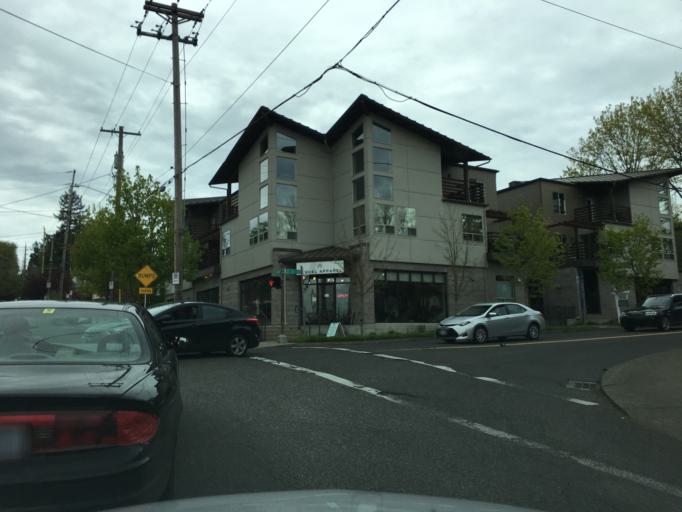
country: US
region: Oregon
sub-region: Multnomah County
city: Lents
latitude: 45.5193
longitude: -122.6023
